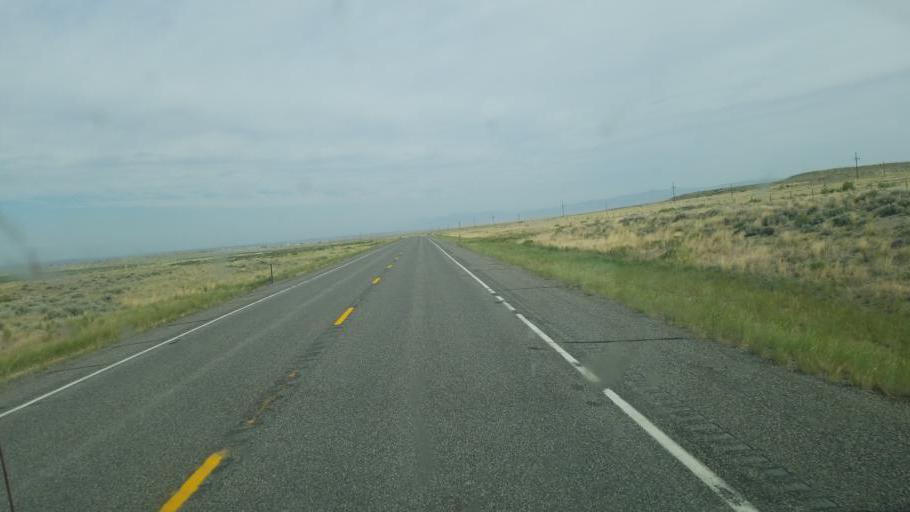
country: US
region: Wyoming
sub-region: Fremont County
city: Riverton
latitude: 43.2279
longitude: -108.0555
